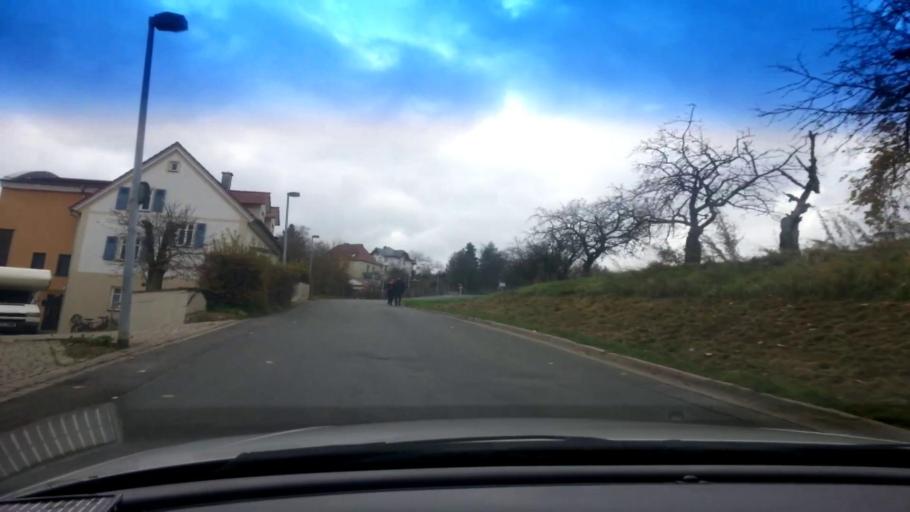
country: DE
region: Bavaria
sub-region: Upper Franconia
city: Bamberg
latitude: 49.8862
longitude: 10.8770
